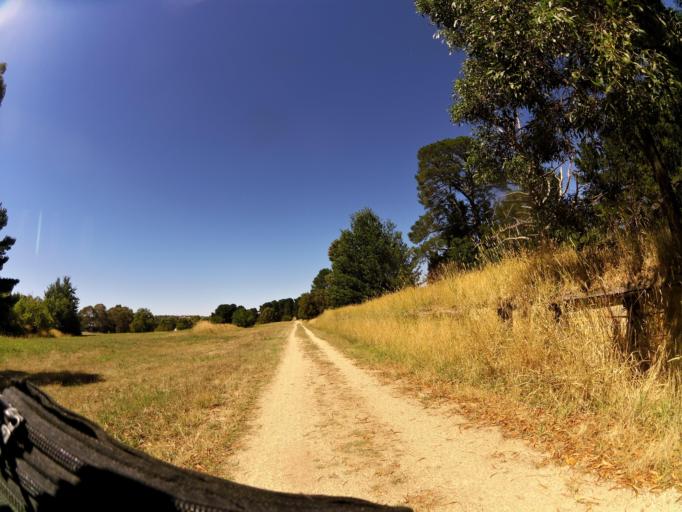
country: AU
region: Victoria
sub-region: Ballarat North
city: Delacombe
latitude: -37.6867
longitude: 143.5662
